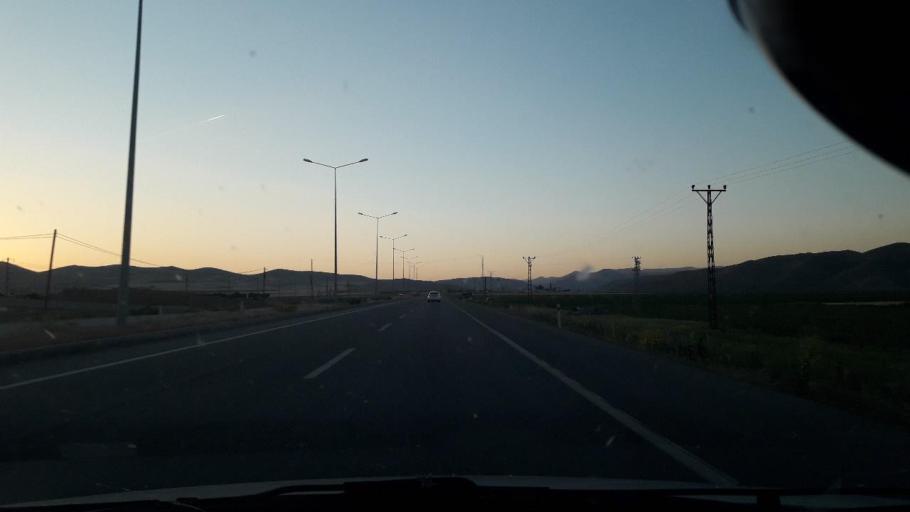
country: TR
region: Malatya
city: Yazihan
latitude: 38.6034
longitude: 38.1797
